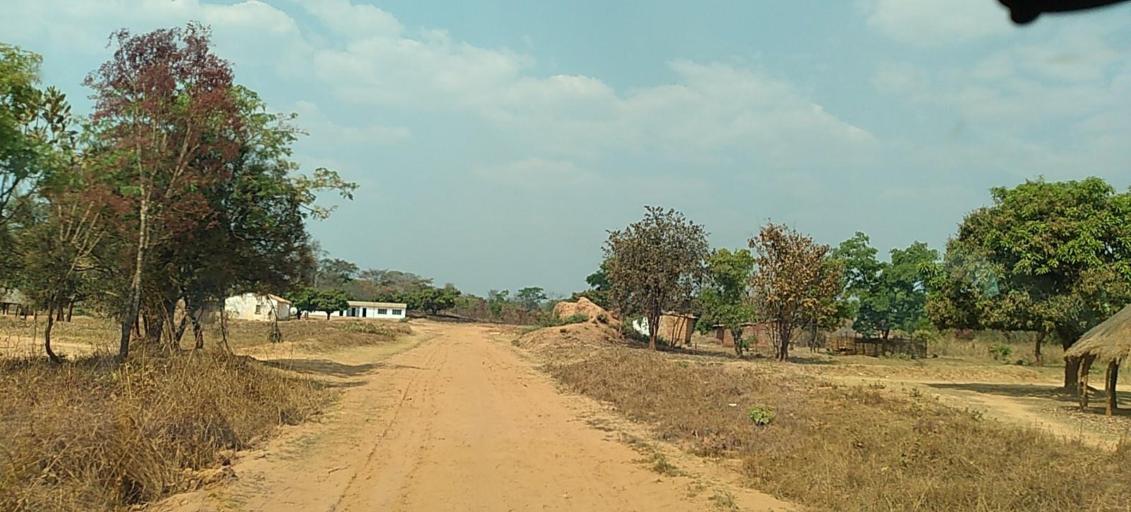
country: ZM
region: North-Western
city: Kasempa
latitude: -13.3049
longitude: 26.0764
